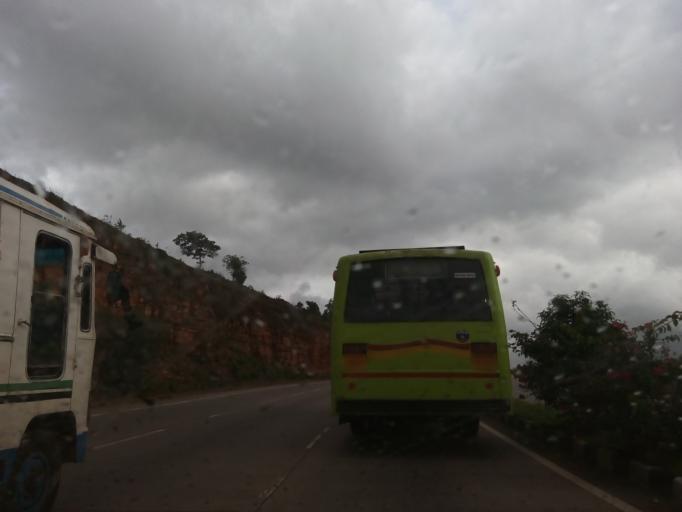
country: IN
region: Karnataka
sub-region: Belgaum
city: Belgaum
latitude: 16.0385
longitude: 74.5307
